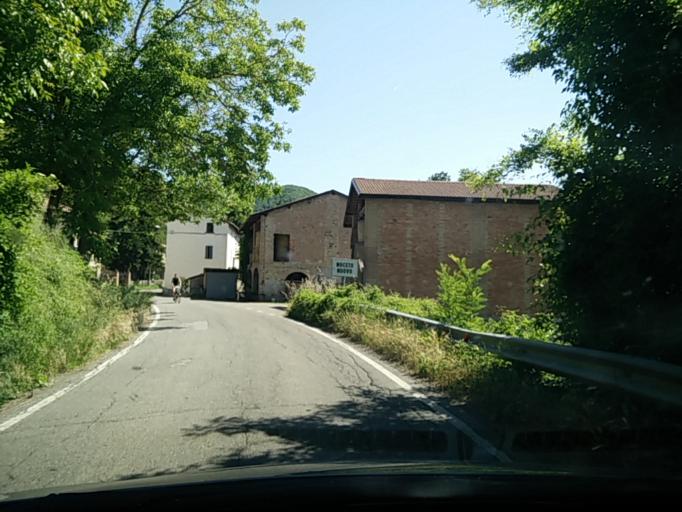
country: IT
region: Lombardy
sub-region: Provincia di Pavia
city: Godiasco
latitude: 44.8946
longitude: 9.0762
